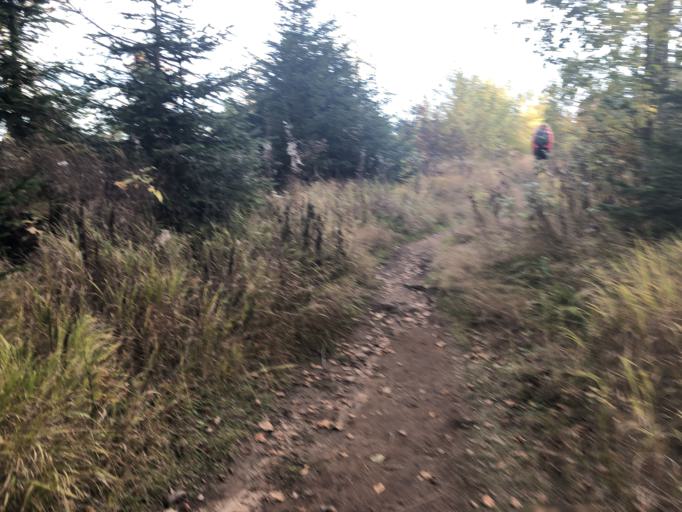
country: DE
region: Bavaria
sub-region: Lower Bavaria
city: Bayerisch Eisenstein
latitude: 49.0770
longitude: 13.1575
